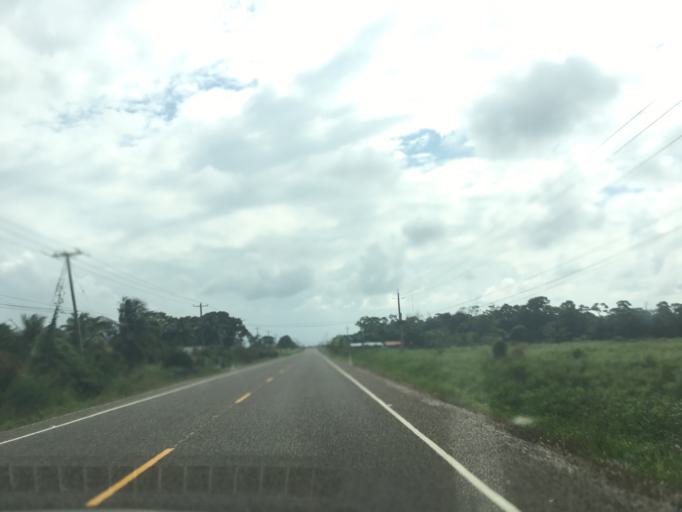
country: BZ
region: Stann Creek
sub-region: Dangriga
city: Dangriga
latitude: 16.9911
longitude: -88.2995
